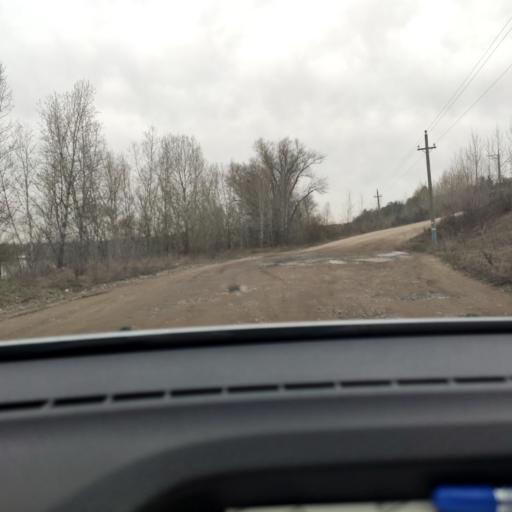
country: RU
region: Bashkortostan
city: Avdon
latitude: 54.6065
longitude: 55.6088
